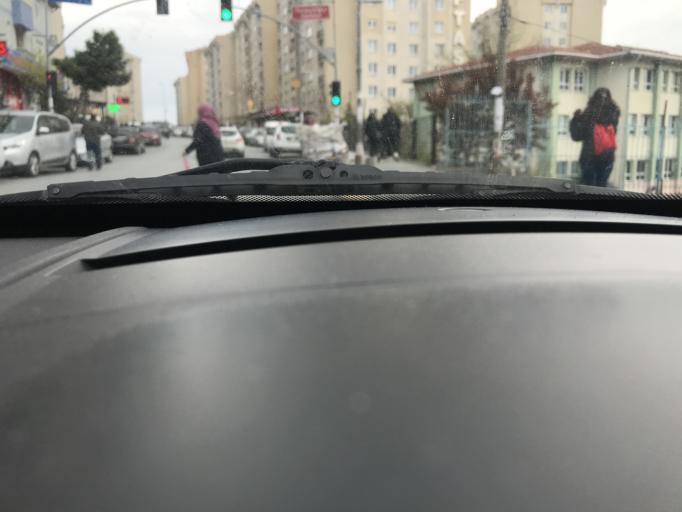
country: TR
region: Istanbul
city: Yakuplu
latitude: 41.0045
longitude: 28.6906
